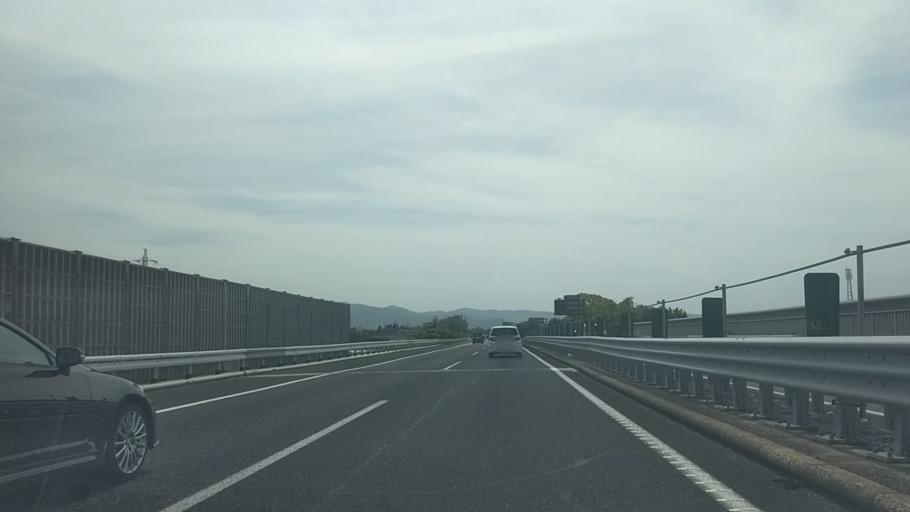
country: JP
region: Aichi
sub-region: Tokai-shi
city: Toyokawa
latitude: 34.8445
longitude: 137.3940
